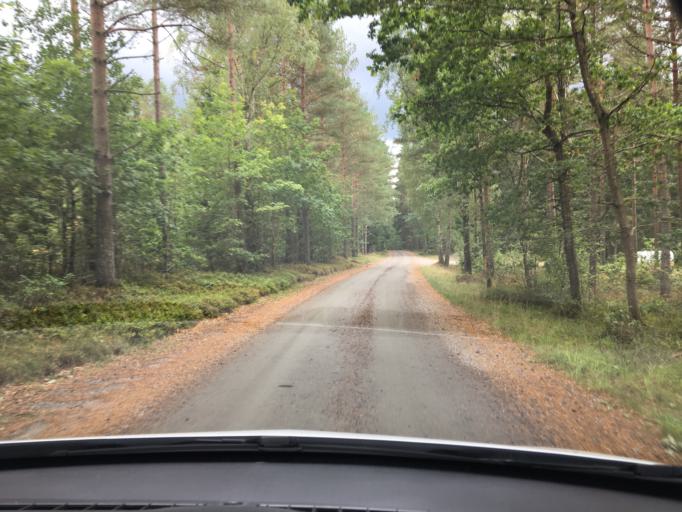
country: SE
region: Vaestra Goetaland
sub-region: Ale Kommun
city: Nodinge-Nol
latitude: 57.8773
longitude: 12.0815
